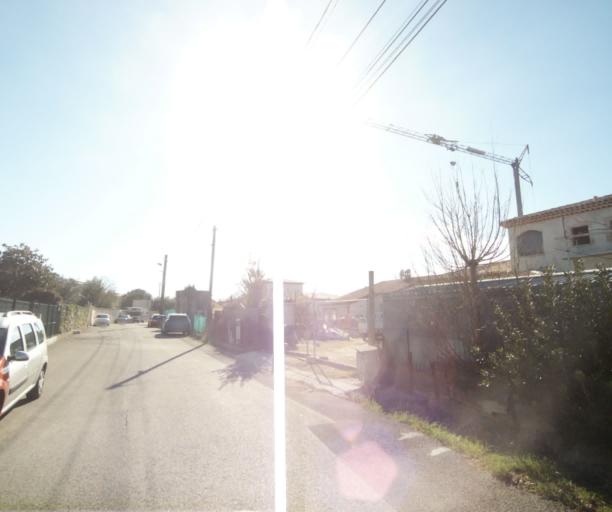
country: FR
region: Provence-Alpes-Cote d'Azur
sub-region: Departement des Alpes-Maritimes
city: Biot
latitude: 43.6086
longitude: 7.1162
